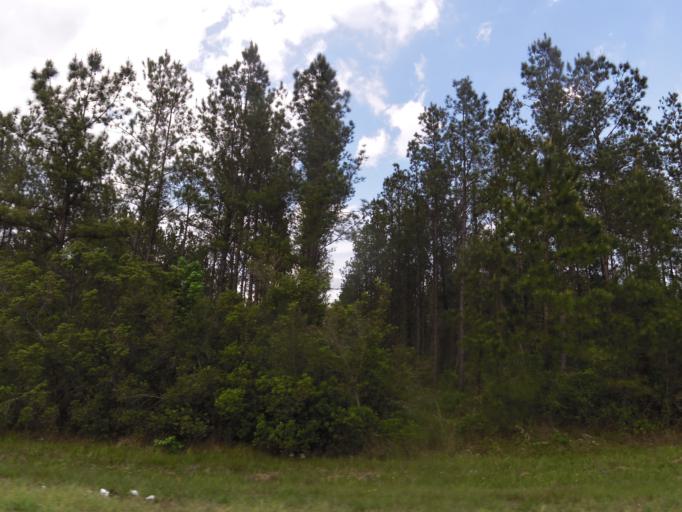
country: US
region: Georgia
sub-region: Camden County
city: Kingsland
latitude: 30.8102
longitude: -81.8339
